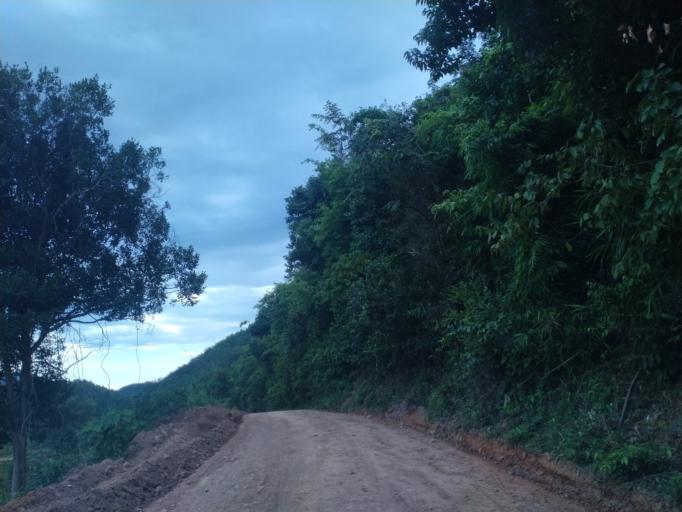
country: TH
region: Nong Khai
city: Rattanawapi
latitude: 18.5446
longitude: 102.9004
